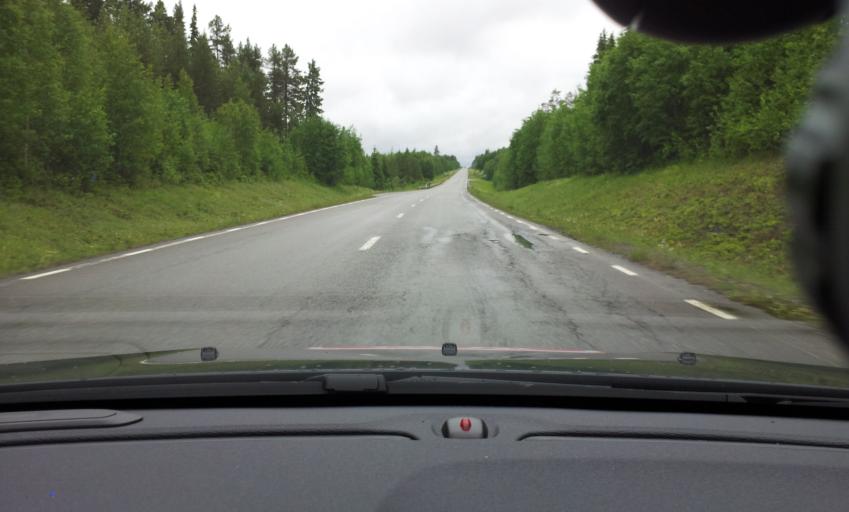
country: SE
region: Jaemtland
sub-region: Krokoms Kommun
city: Krokom
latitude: 63.4141
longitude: 14.4918
